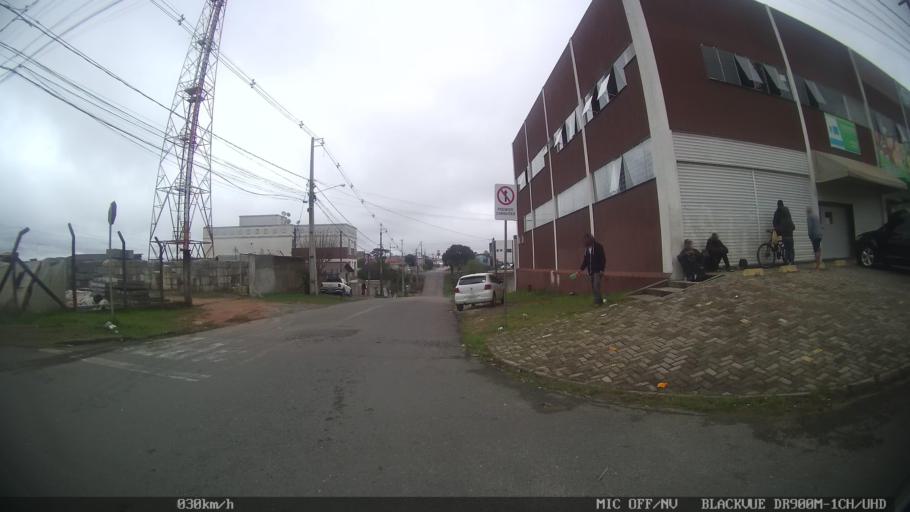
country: BR
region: Parana
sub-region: Sao Jose Dos Pinhais
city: Sao Jose dos Pinhais
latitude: -25.6107
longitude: -49.1701
